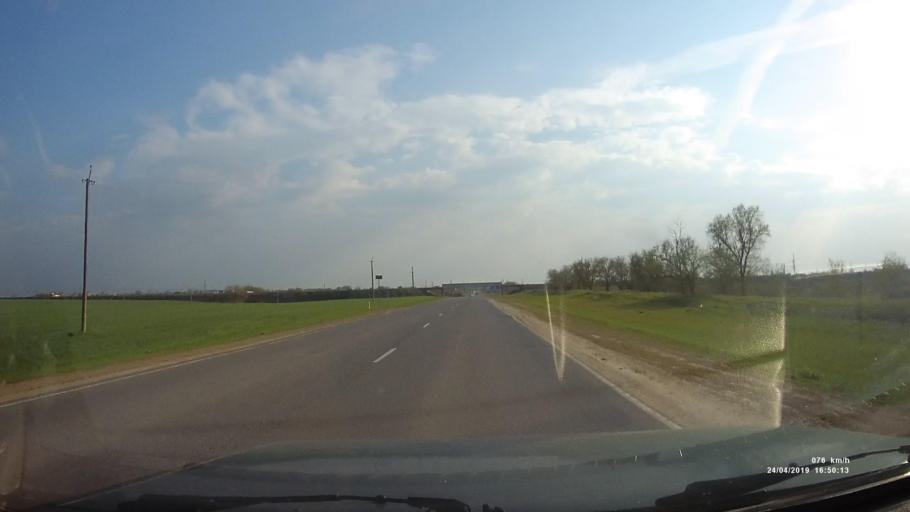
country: RU
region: Rostov
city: Proletarsk
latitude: 46.7081
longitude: 41.7566
